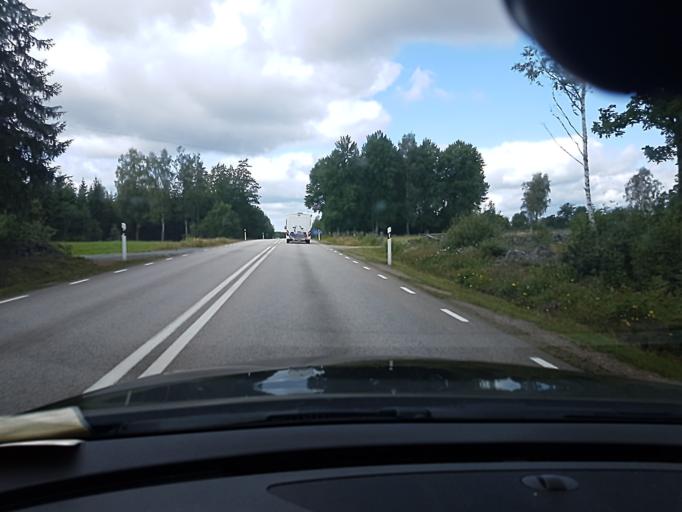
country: SE
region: Kronoberg
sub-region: Lessebo Kommun
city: Lessebo
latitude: 56.7298
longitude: 15.3529
